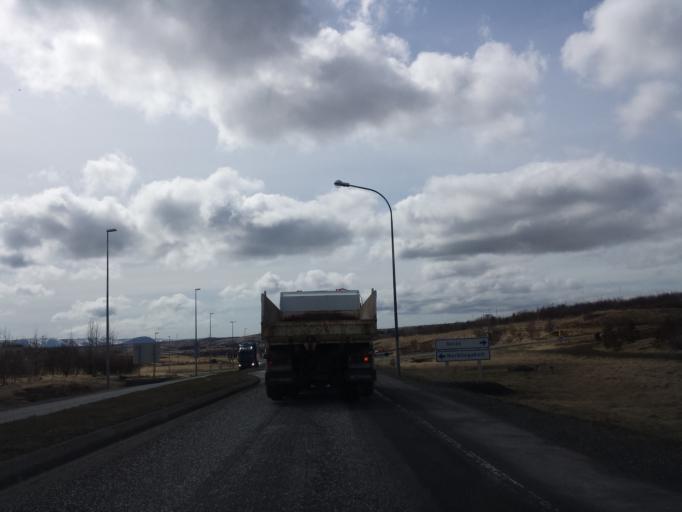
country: IS
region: Capital Region
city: Mosfellsbaer
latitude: 64.1022
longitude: -21.7788
